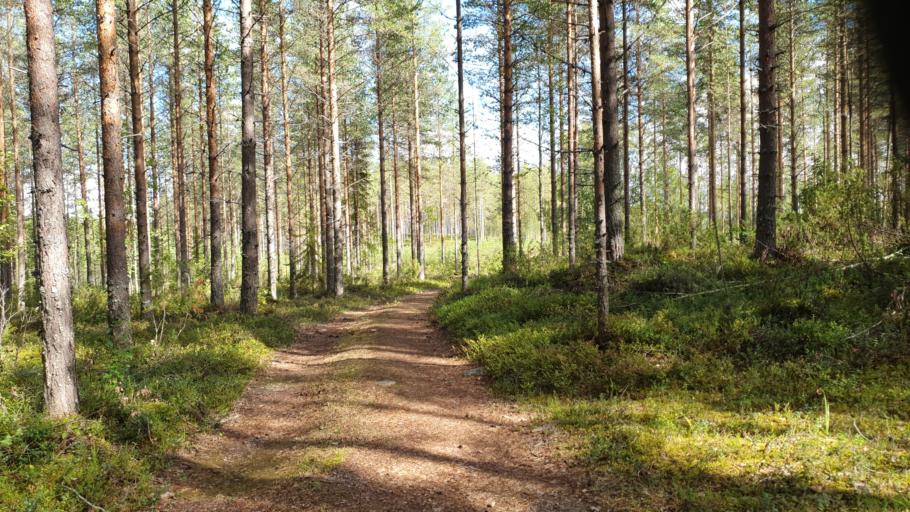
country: FI
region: Kainuu
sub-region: Kehys-Kainuu
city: Kuhmo
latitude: 64.1467
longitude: 29.3415
